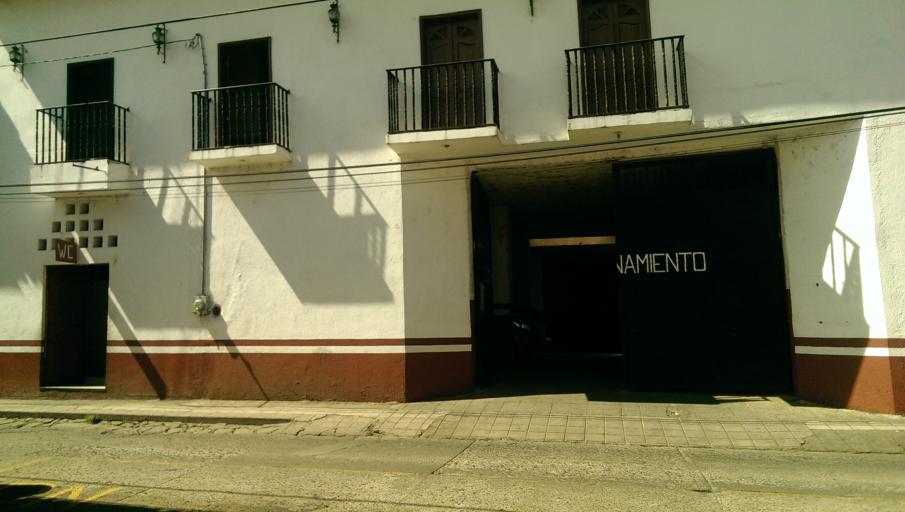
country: MX
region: Michoacan
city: Quiroga
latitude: 19.6648
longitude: -101.5224
